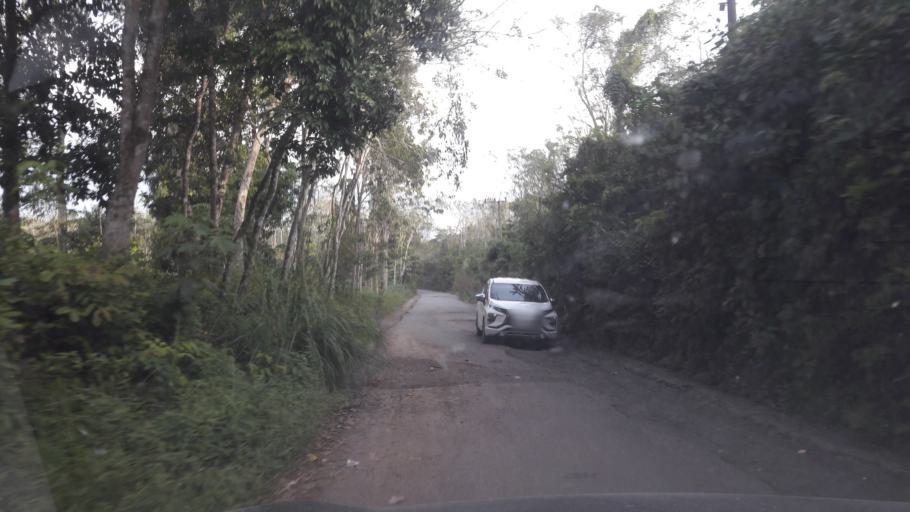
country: ID
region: South Sumatra
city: Gunungmenang
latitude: -3.3102
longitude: 104.0921
